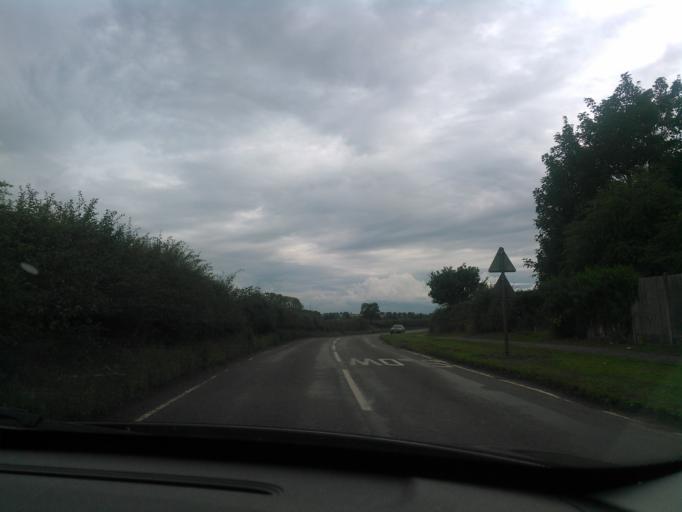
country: GB
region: England
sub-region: Shropshire
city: Wem
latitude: 52.8627
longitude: -2.7022
